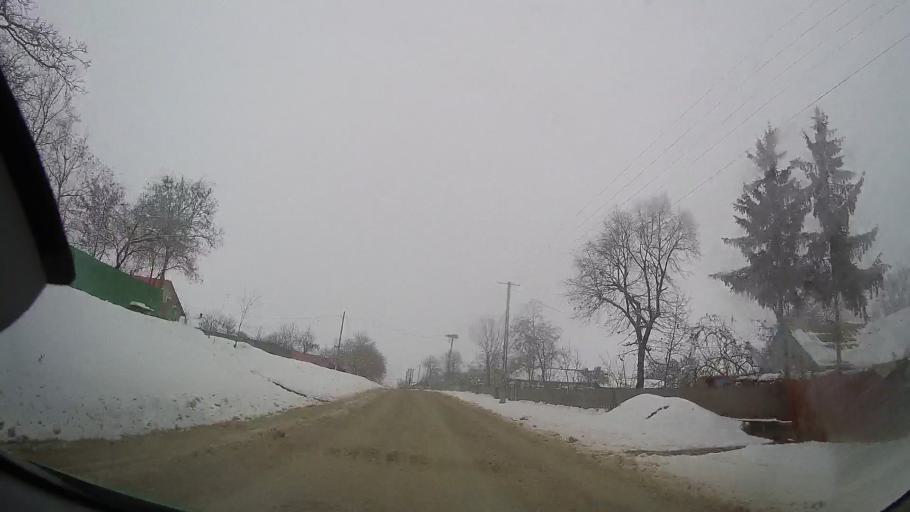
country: RO
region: Vaslui
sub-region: Comuna Todiresti
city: Todiresti
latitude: 46.8769
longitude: 27.3755
